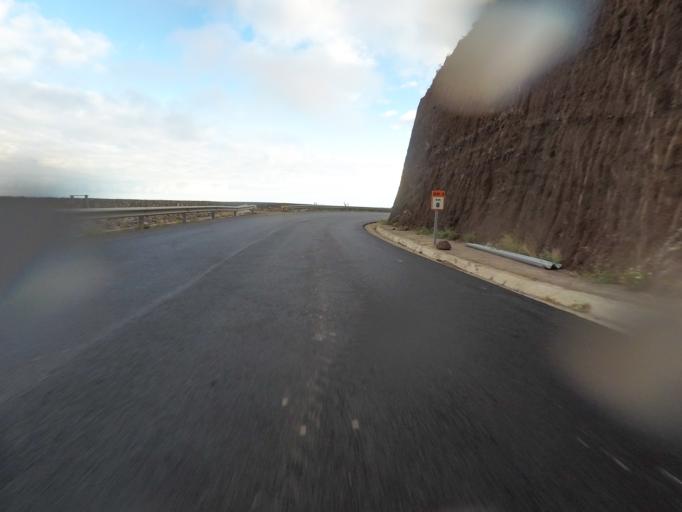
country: ES
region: Canary Islands
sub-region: Provincia de Santa Cruz de Tenerife
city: Alajero
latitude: 28.0593
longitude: -17.2026
